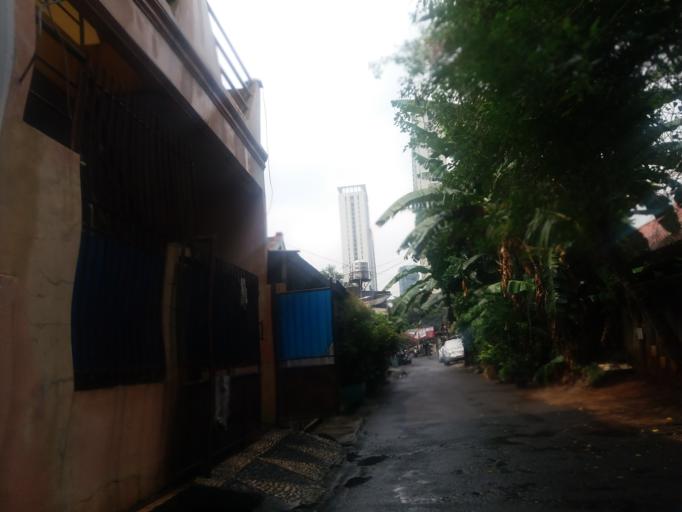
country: ID
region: Jakarta Raya
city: Jakarta
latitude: -6.2157
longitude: 106.8250
